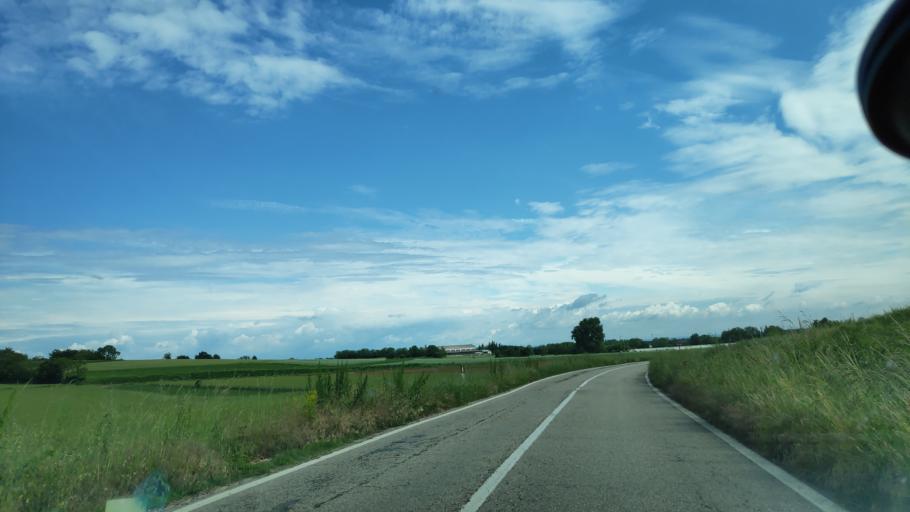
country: IT
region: Piedmont
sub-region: Provincia di Torino
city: Cambiano
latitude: 44.9890
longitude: 7.7788
